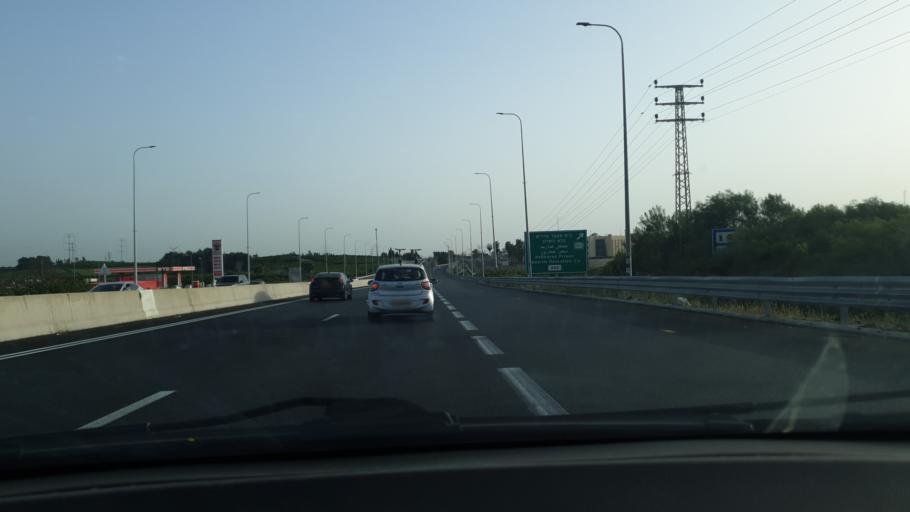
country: IL
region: Central District
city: Even Yehuda
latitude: 32.2452
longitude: 34.8881
